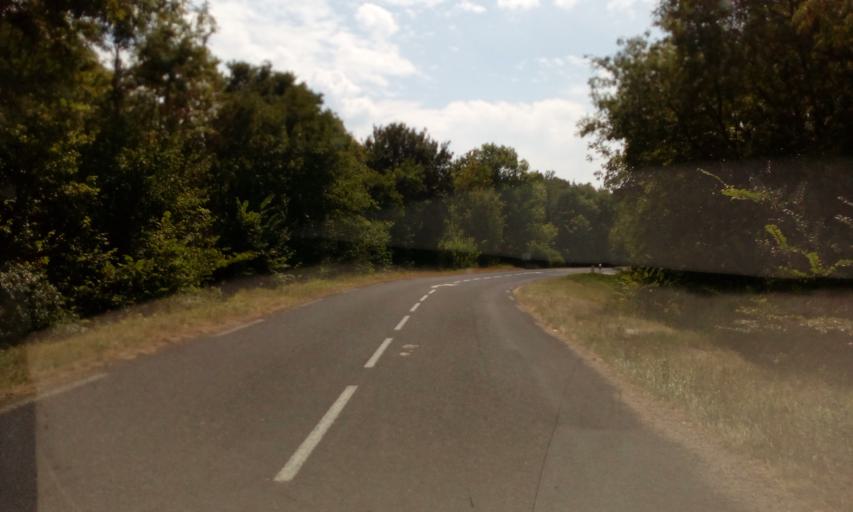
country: FR
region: Lorraine
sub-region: Departement de Meurthe-et-Moselle
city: Montauville
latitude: 48.9405
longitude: 5.8861
